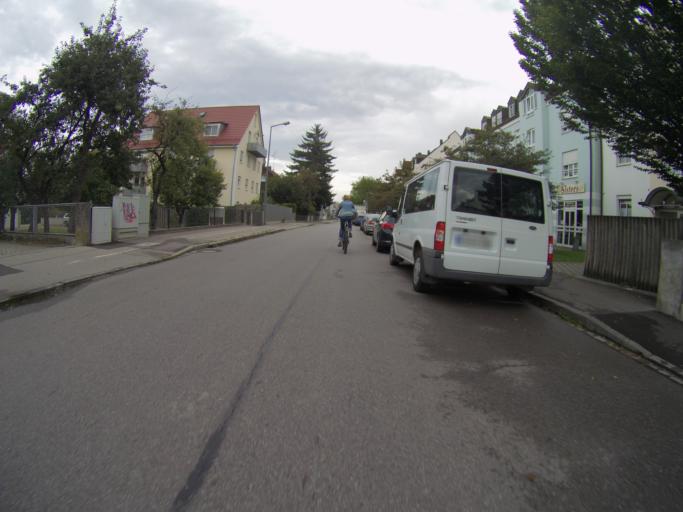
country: DE
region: Bavaria
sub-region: Upper Bavaria
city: Freising
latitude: 48.3959
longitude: 11.7551
